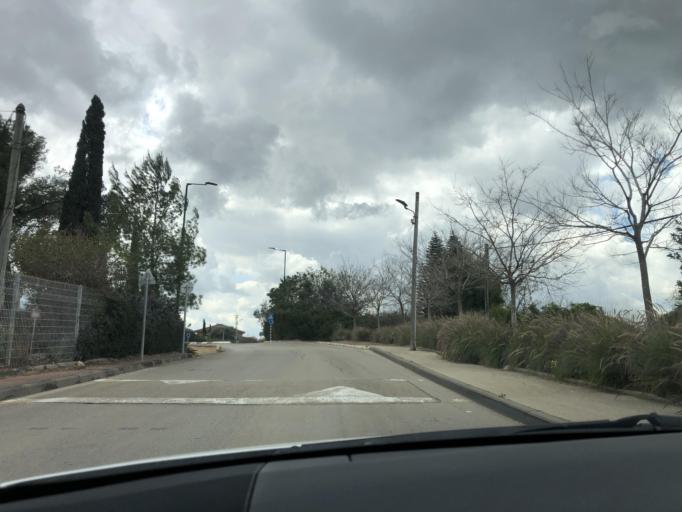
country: IL
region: Central District
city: Tel Mond
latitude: 32.2688
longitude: 34.9353
